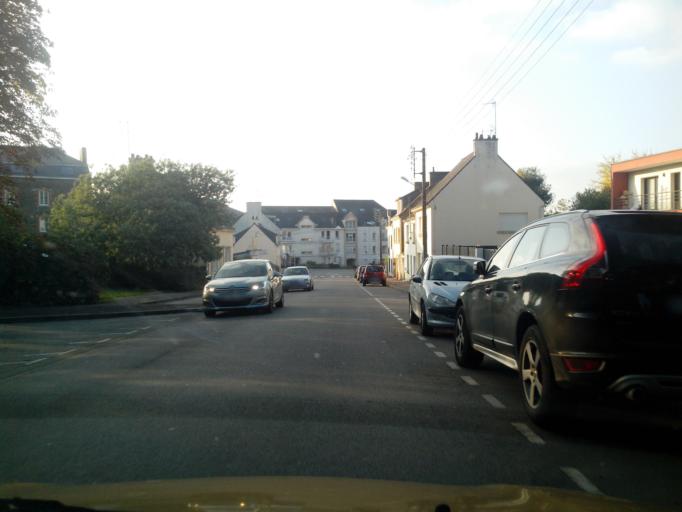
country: FR
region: Brittany
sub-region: Departement du Morbihan
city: Ploermel
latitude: 47.9341
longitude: -2.3975
